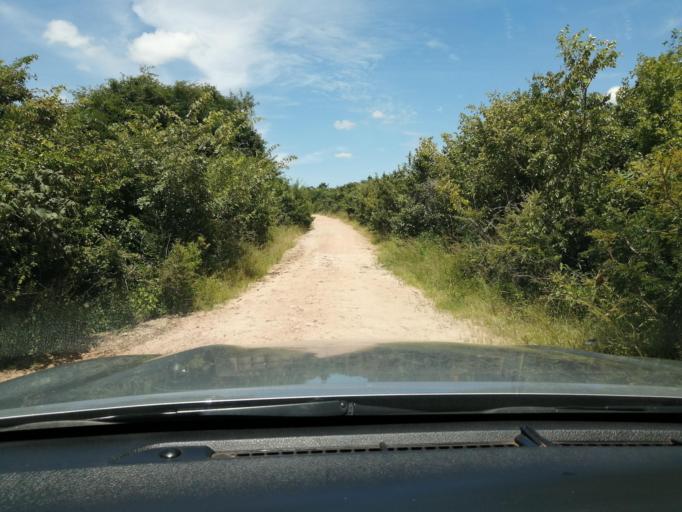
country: ZM
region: Central
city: Chibombo
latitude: -15.1050
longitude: 27.8516
